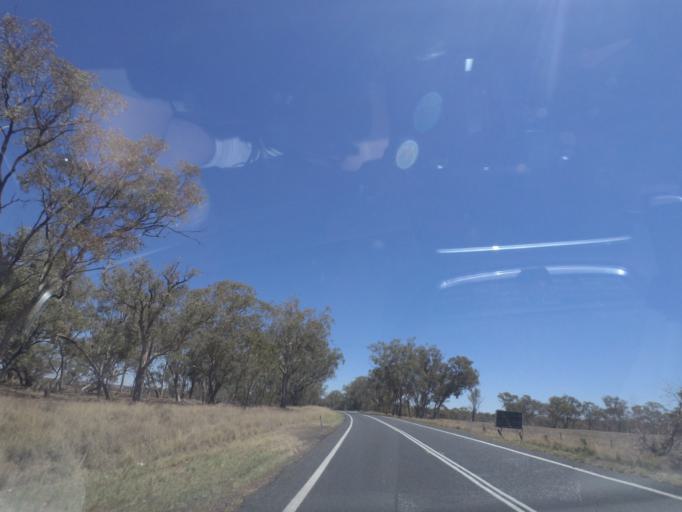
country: AU
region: New South Wales
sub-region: Warrumbungle Shire
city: Coonabarabran
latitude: -31.4172
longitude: 149.2253
